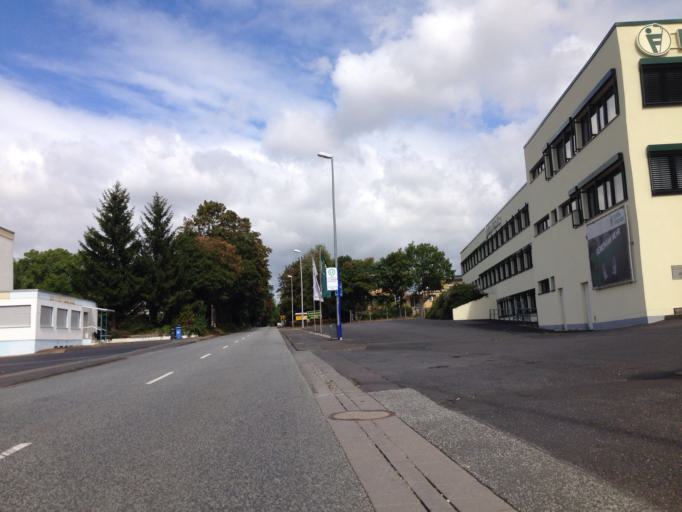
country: DE
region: Hesse
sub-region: Regierungsbezirk Giessen
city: Limburg an der Lahn
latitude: 50.4073
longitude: 8.0619
